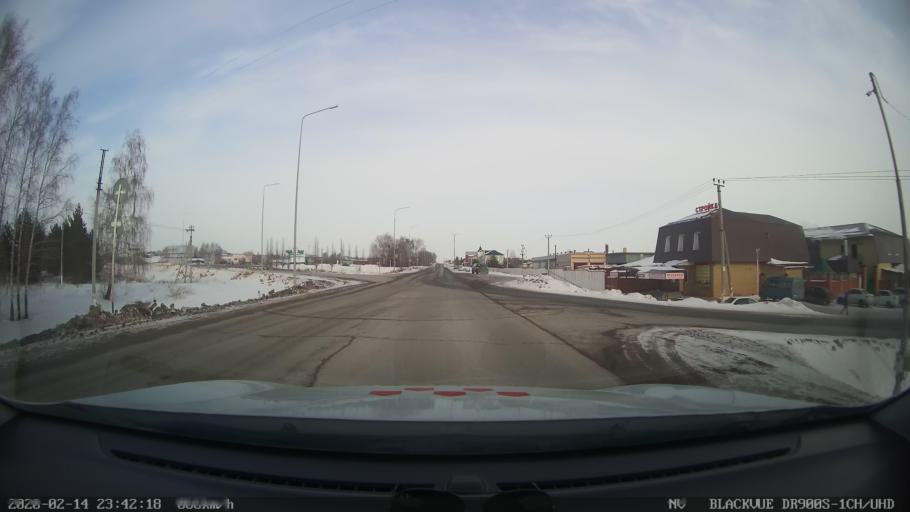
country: RU
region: Tatarstan
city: Kuybyshevskiy Zaton
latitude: 55.1907
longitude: 49.2469
